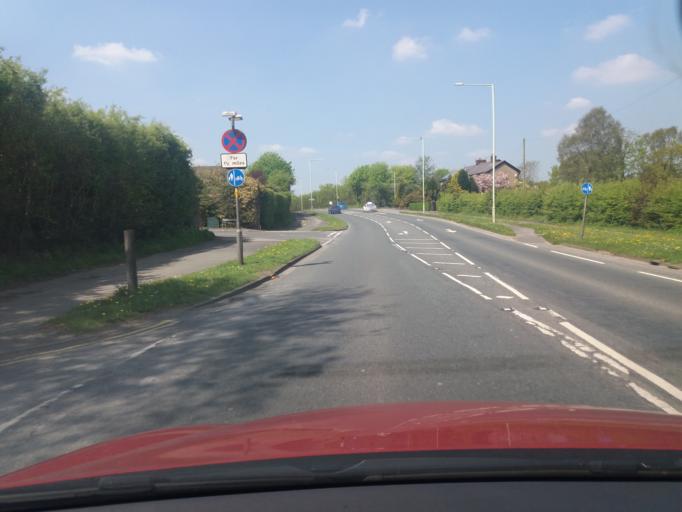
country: GB
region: England
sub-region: Lancashire
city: Euxton
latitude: 53.6683
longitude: -2.6438
